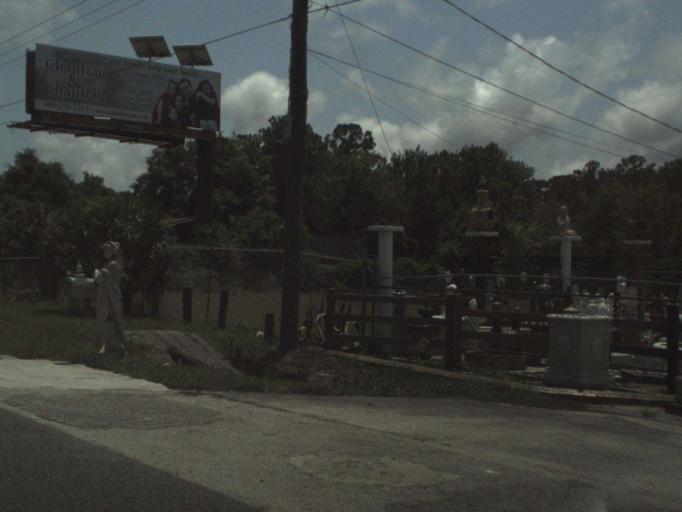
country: US
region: Florida
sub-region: Volusia County
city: Ormond-by-the-Sea
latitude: 29.3150
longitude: -81.1048
